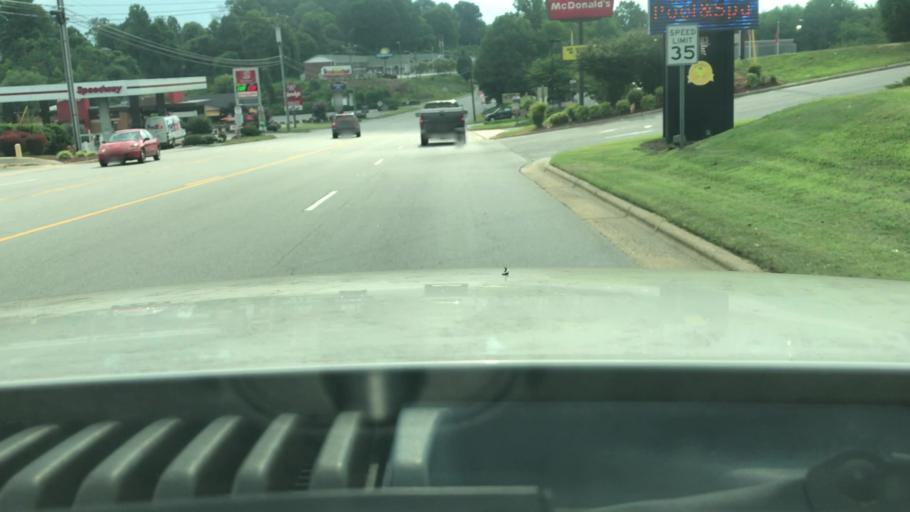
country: US
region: North Carolina
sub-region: Yadkin County
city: Jonesville
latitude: 36.2393
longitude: -80.8194
